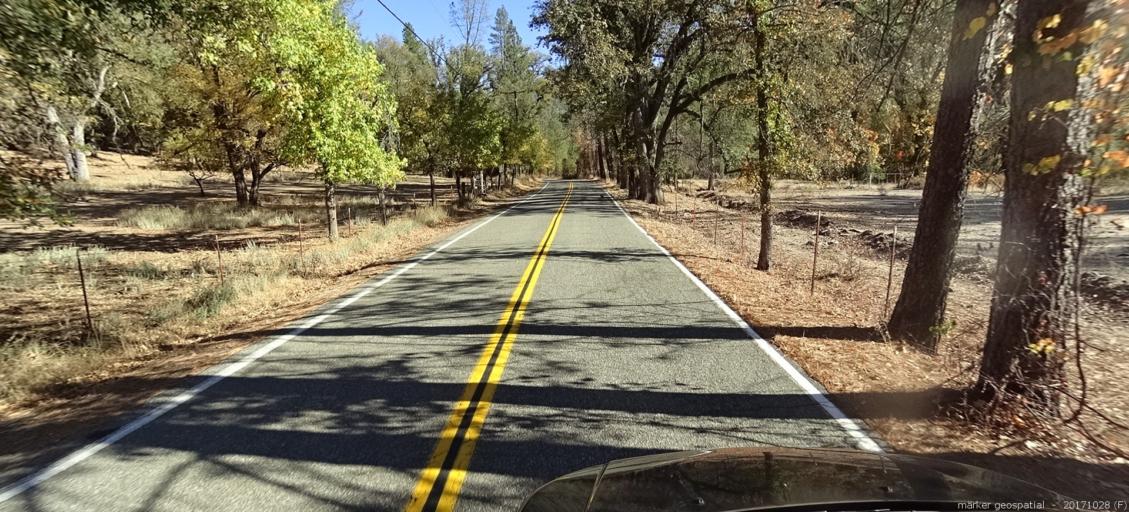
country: US
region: California
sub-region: Trinity County
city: Lewiston
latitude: 40.7505
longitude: -122.6185
